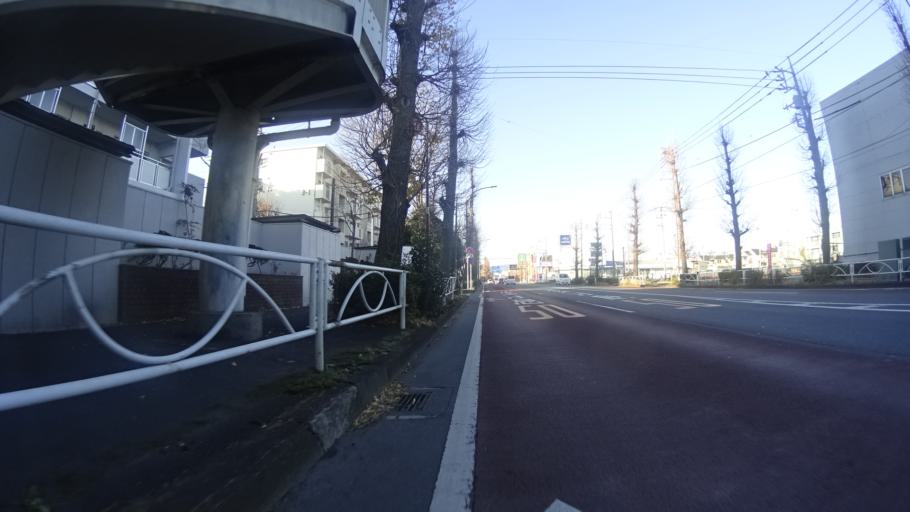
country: JP
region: Tokyo
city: Hino
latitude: 35.6652
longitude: 139.3620
